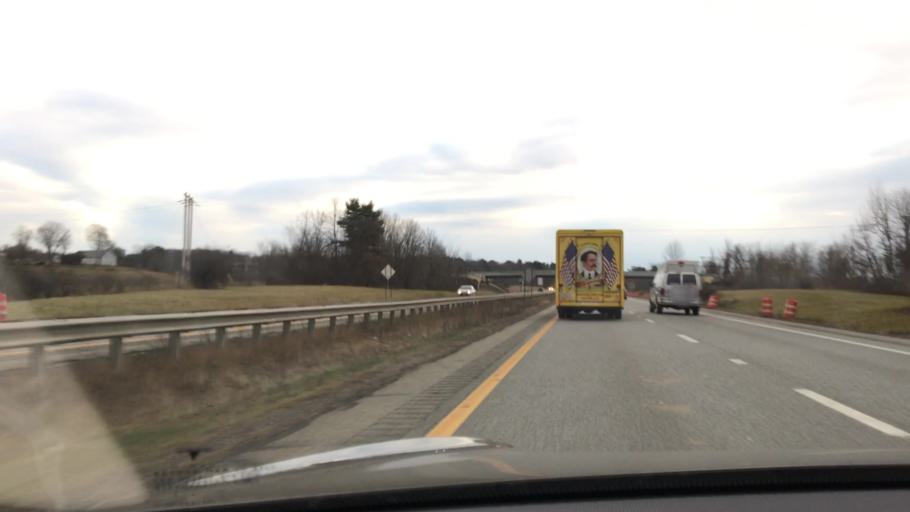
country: US
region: Maine
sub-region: Kennebec County
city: Hallowell
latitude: 44.2999
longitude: -69.8076
